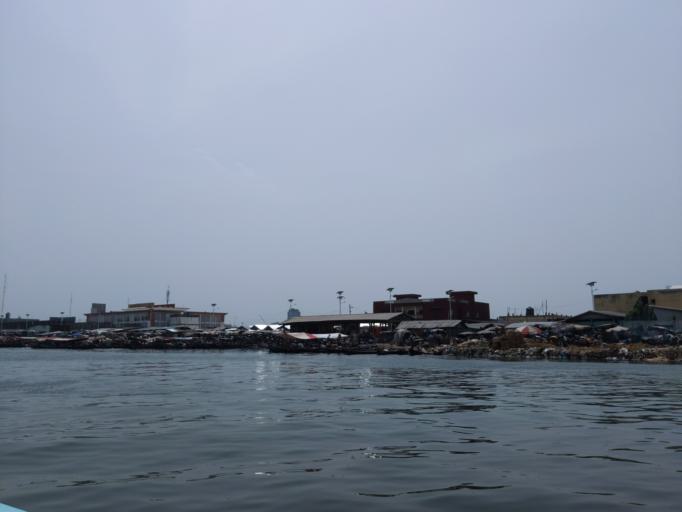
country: BJ
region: Littoral
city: Cotonou
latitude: 6.3745
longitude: 2.4360
